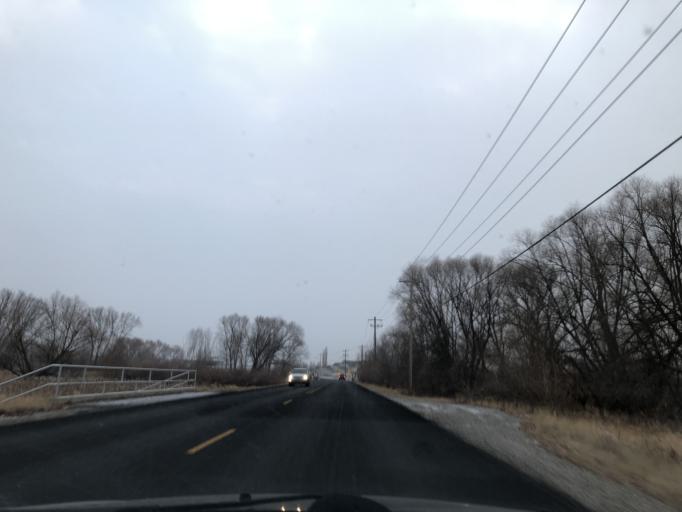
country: US
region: Utah
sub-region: Cache County
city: Logan
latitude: 41.7076
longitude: -111.8531
